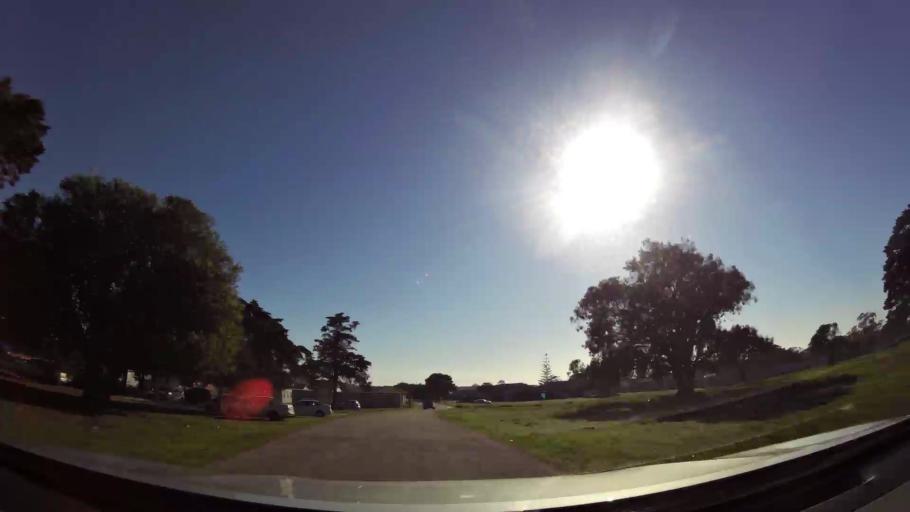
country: ZA
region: Eastern Cape
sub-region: Nelson Mandela Bay Metropolitan Municipality
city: Port Elizabeth
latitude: -33.9864
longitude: 25.6281
